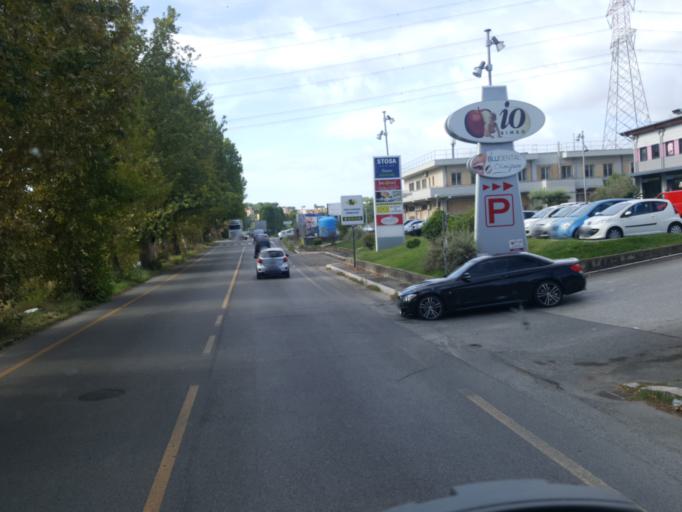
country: IT
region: Latium
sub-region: Citta metropolitana di Roma Capitale
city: Bivio di Capanelle
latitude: 42.1150
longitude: 12.5876
